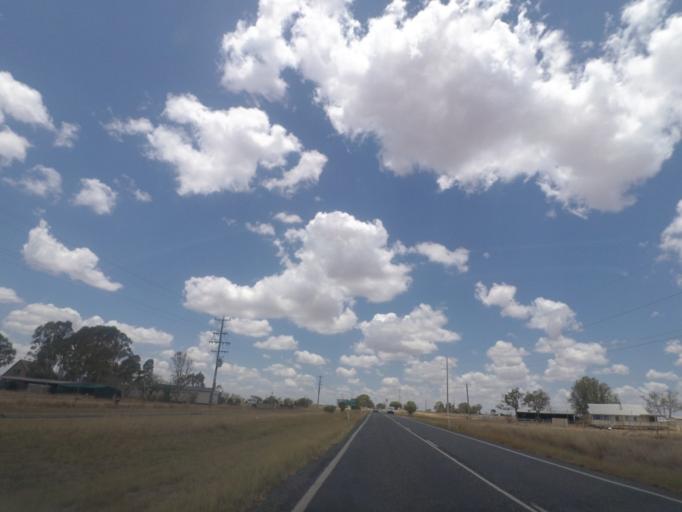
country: AU
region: Queensland
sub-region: Southern Downs
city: Warwick
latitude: -27.9290
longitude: 151.9854
